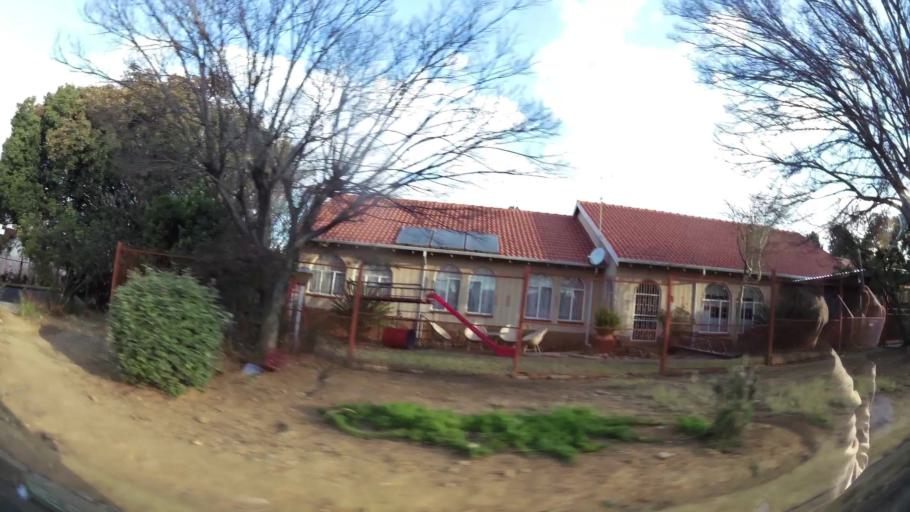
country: ZA
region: Gauteng
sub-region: West Rand District Municipality
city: Krugersdorp
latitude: -26.0726
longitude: 27.7649
